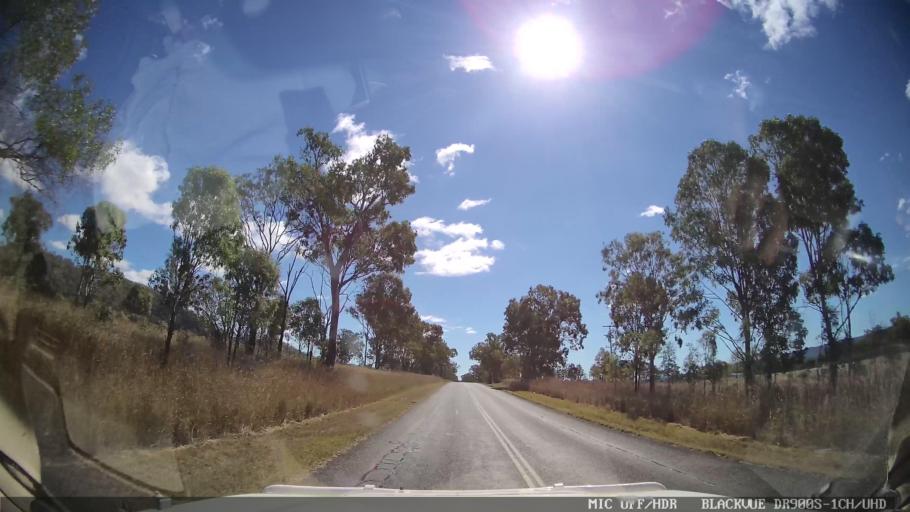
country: AU
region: Queensland
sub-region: Gladstone
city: Toolooa
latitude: -24.4538
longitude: 151.3468
